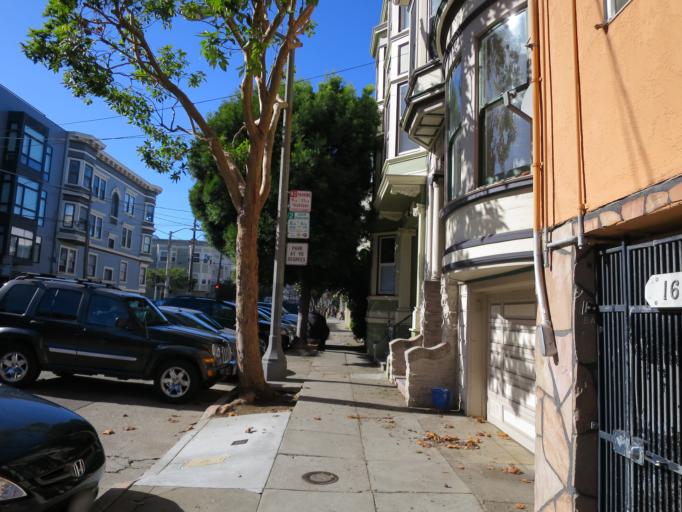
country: US
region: California
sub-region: San Francisco County
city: San Francisco
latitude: 37.7762
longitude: -122.4441
